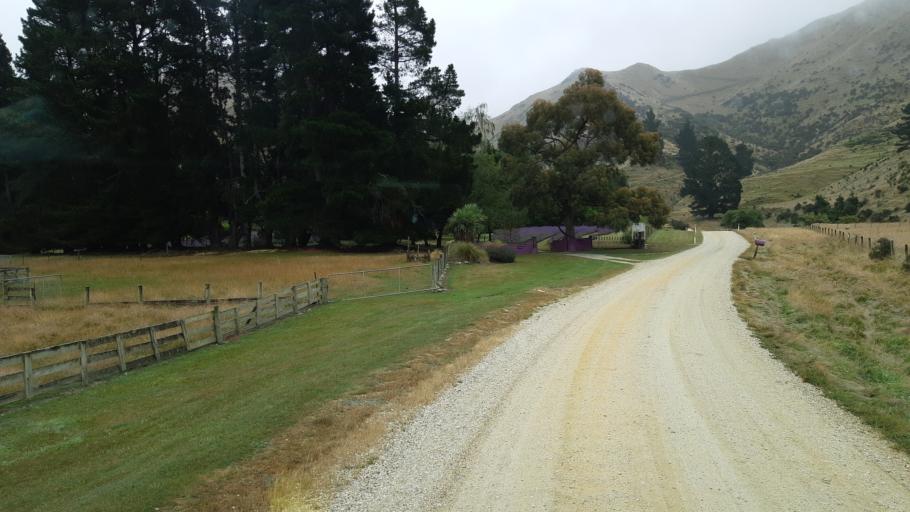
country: NZ
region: Otago
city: Oamaru
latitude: -44.9544
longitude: 170.4752
